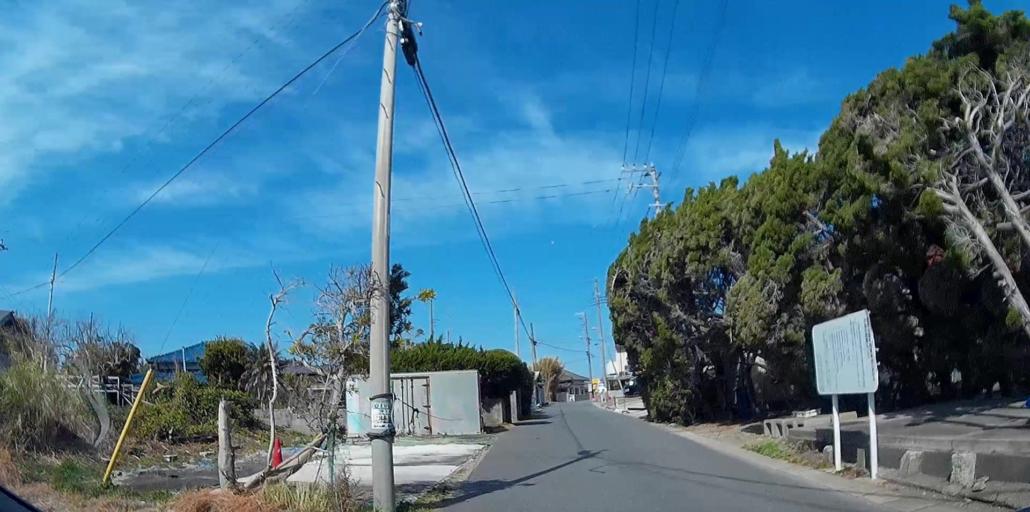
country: JP
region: Chiba
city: Tateyama
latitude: 34.9748
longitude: 139.7570
